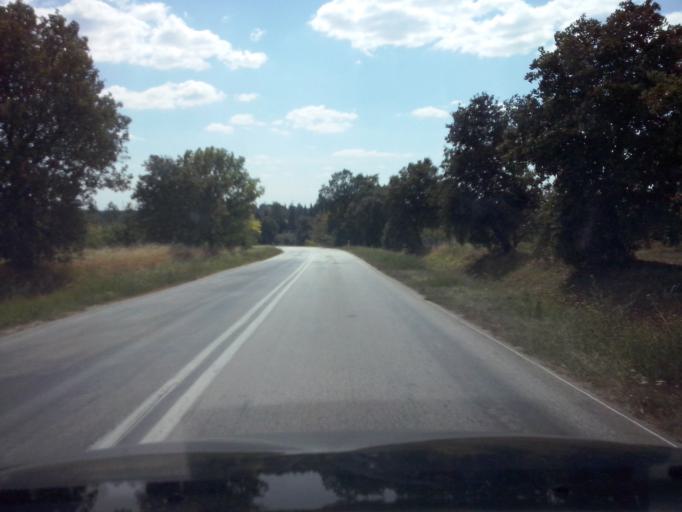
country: PL
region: Swietokrzyskie
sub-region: Powiat staszowski
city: Szydlow
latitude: 50.6011
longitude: 21.0086
